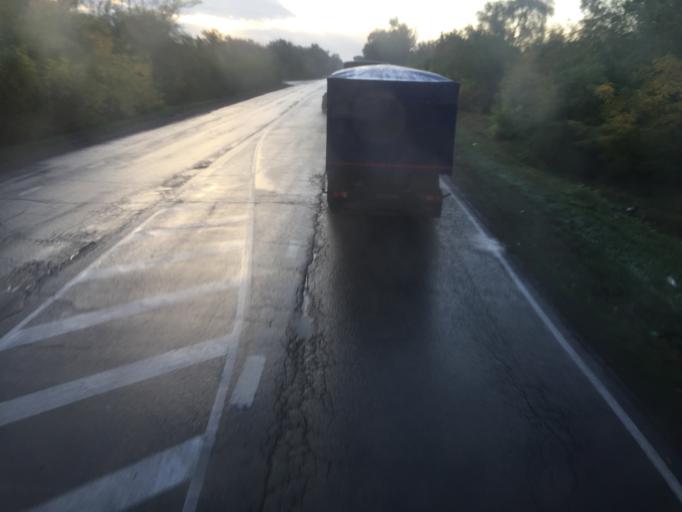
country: RU
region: Rostov
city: Bataysk
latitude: 47.0325
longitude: 39.8747
